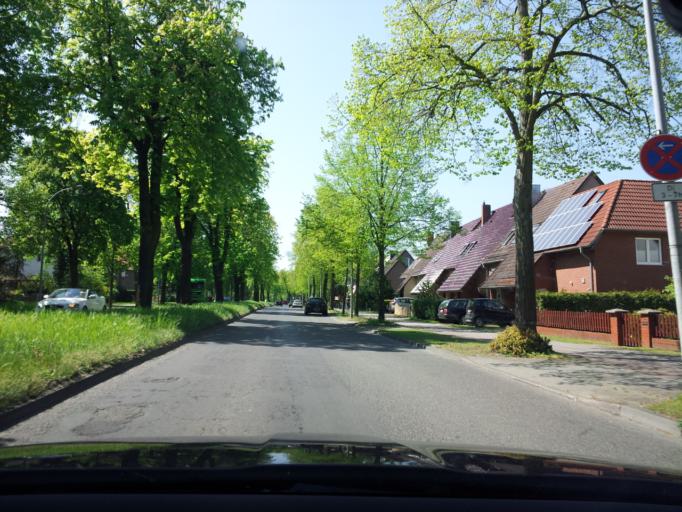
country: DE
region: Brandenburg
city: Teltow
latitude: 52.4079
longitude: 13.2879
